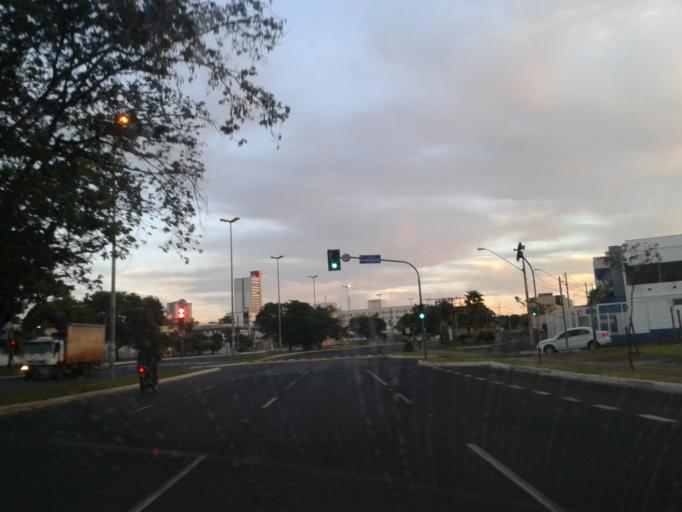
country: BR
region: Minas Gerais
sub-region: Uberlandia
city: Uberlandia
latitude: -18.9037
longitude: -48.2607
